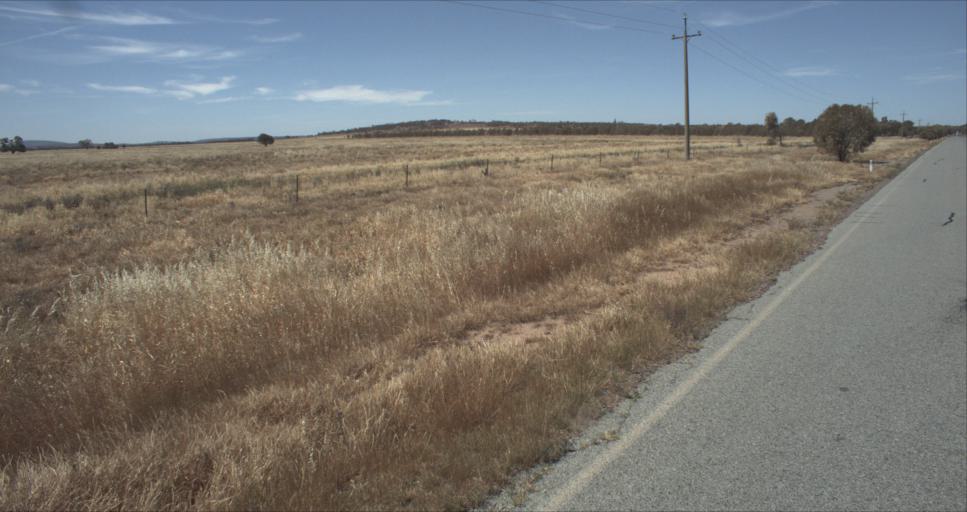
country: AU
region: New South Wales
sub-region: Leeton
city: Leeton
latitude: -34.6308
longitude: 146.4563
